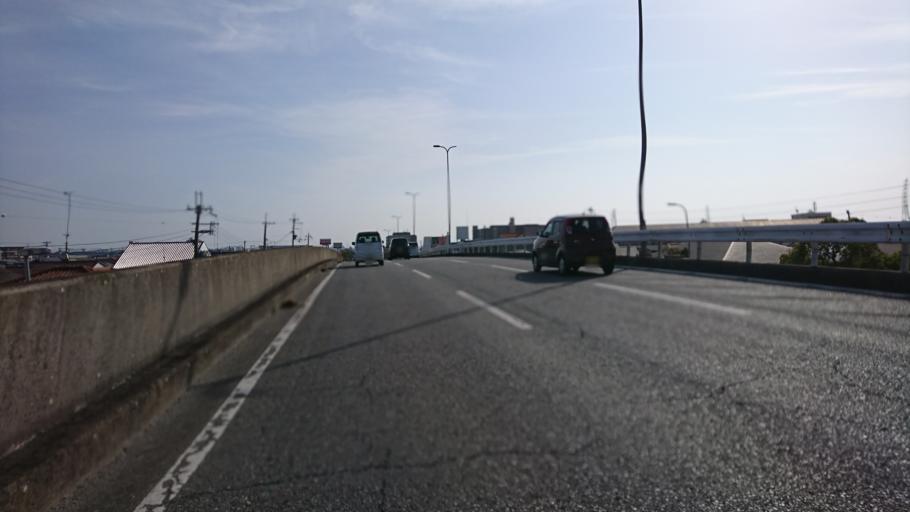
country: JP
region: Hyogo
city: Kakogawacho-honmachi
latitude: 34.7397
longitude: 134.8462
